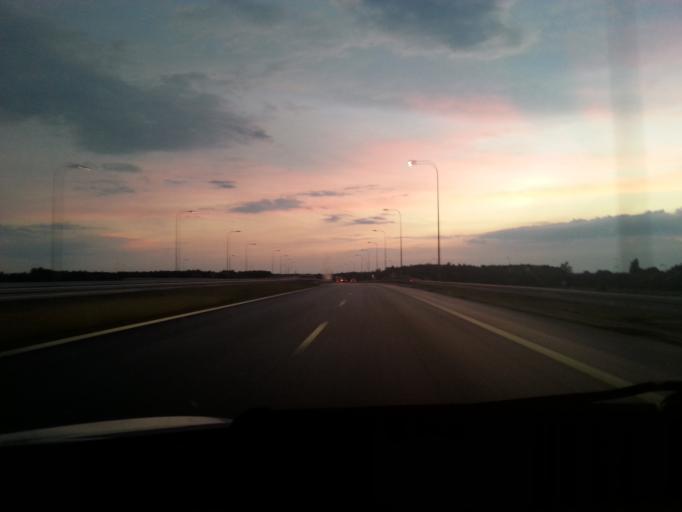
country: PL
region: Lodz Voivodeship
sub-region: Powiat zdunskowolski
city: Zapolice
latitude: 51.5971
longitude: 18.8760
